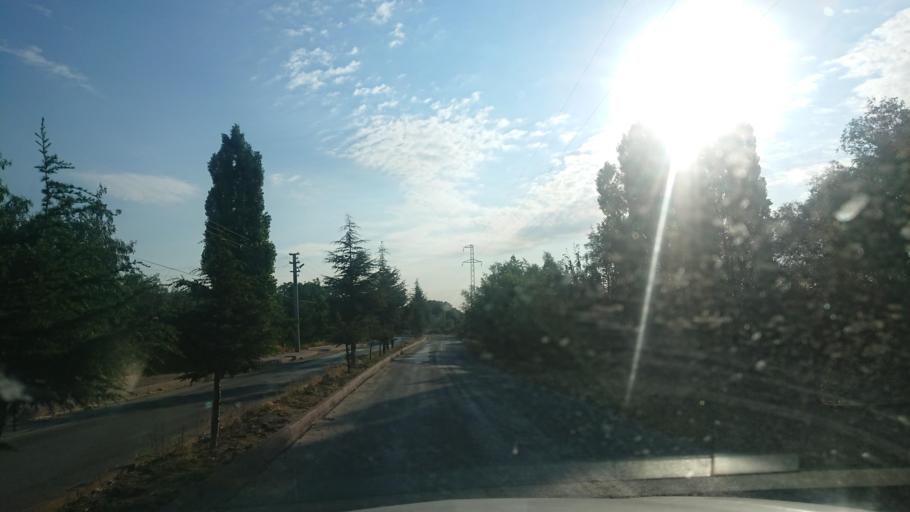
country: TR
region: Aksaray
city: Ortakoy
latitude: 38.7491
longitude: 34.0538
